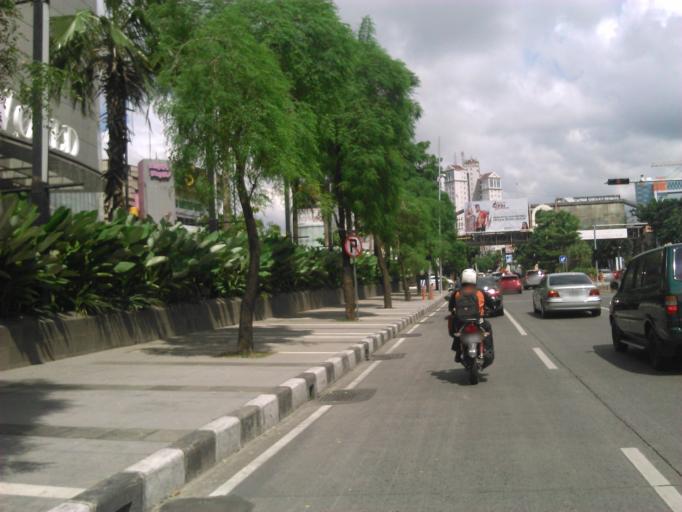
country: ID
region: East Java
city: Jagirsidosermo
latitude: -7.2919
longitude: 112.7194
